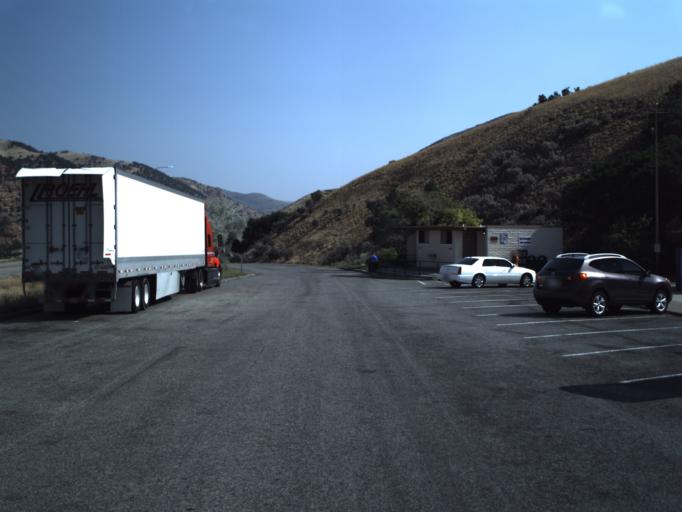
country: US
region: Utah
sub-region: Summit County
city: Coalville
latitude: 40.9896
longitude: -111.4031
